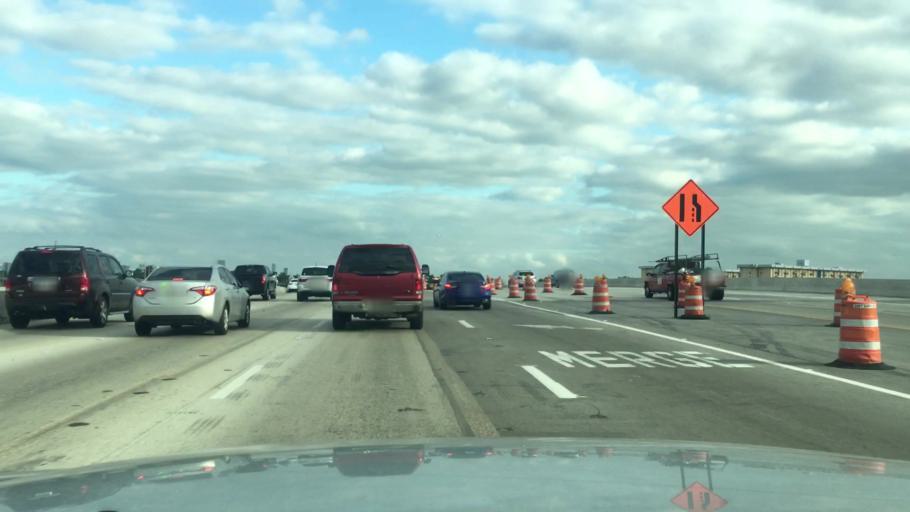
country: US
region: Florida
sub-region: Miami-Dade County
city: West Miami
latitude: 25.7840
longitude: -80.2759
